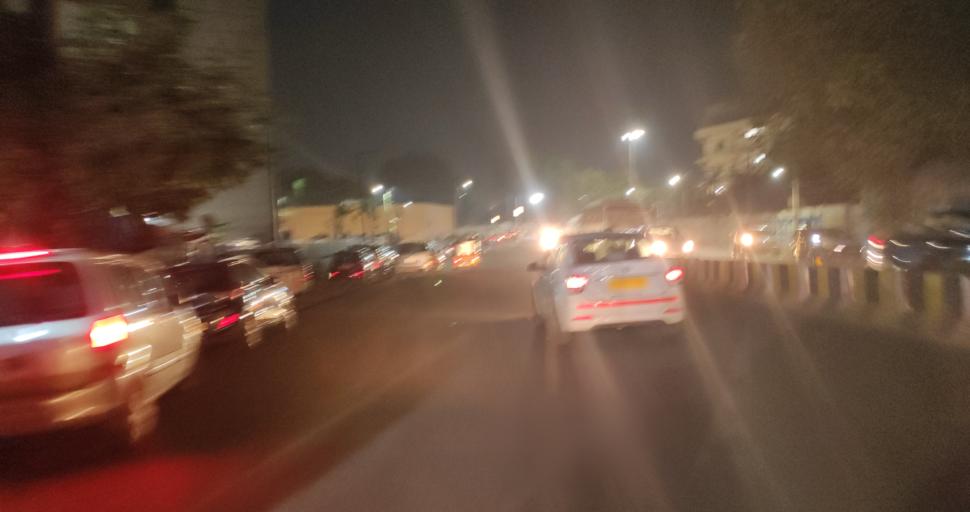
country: IN
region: Telangana
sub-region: Rangareddi
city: Gaddi Annaram
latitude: 17.3638
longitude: 78.5023
